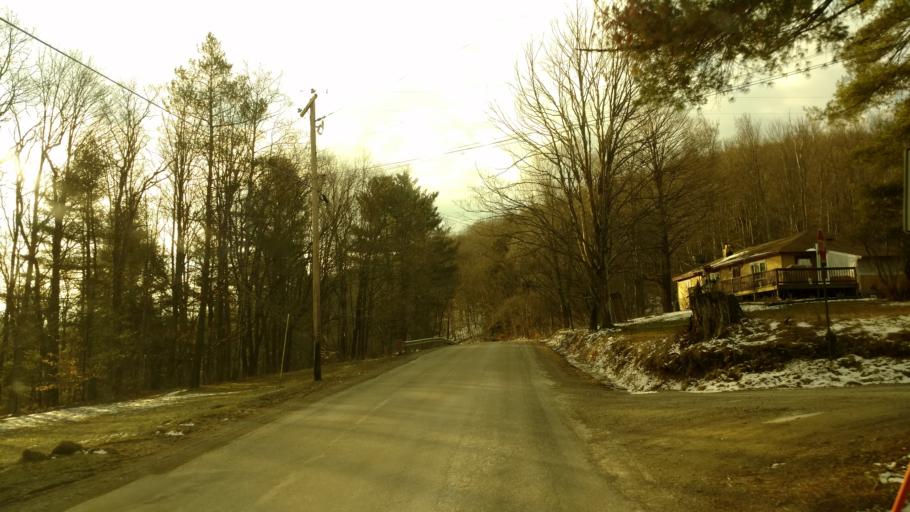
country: US
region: New York
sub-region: Allegany County
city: Andover
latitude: 41.9468
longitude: -77.8242
